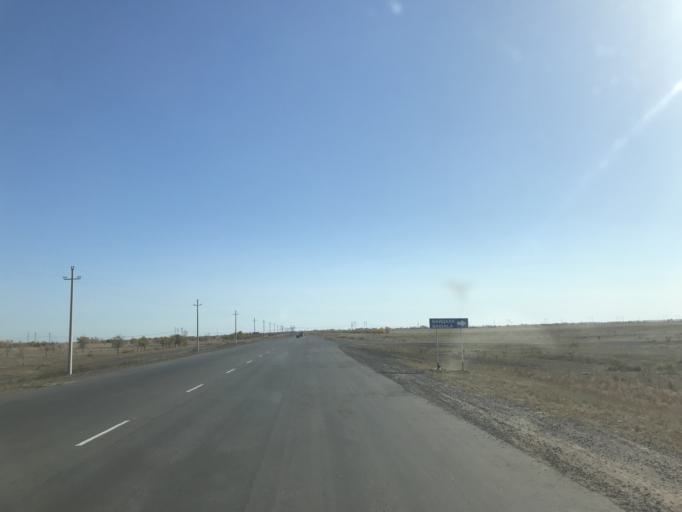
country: KZ
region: Pavlodar
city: Pavlodar
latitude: 52.1450
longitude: 77.0676
